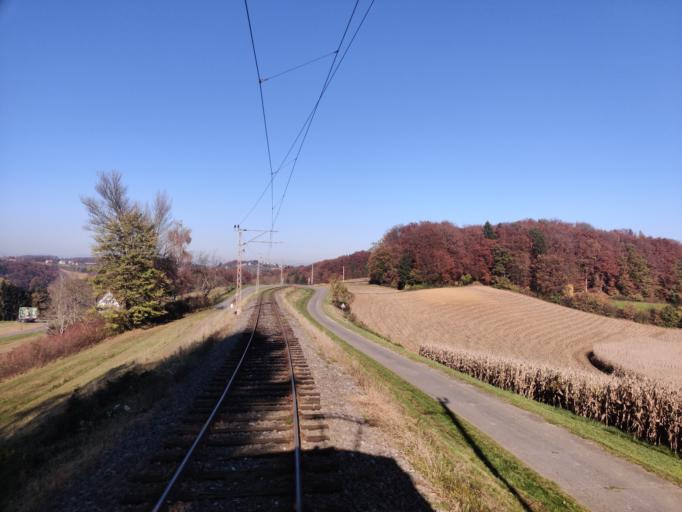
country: AT
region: Styria
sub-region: Politischer Bezirk Suedoststeiermark
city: Maierdorf
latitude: 46.9090
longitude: 15.8390
